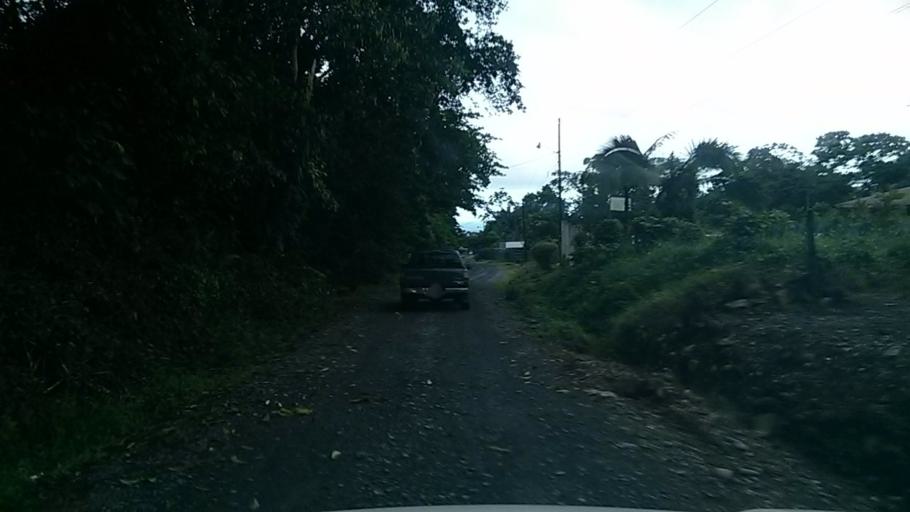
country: CR
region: Limon
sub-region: Canton de Pococi
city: Guapiles
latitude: 10.1692
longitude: -83.7836
